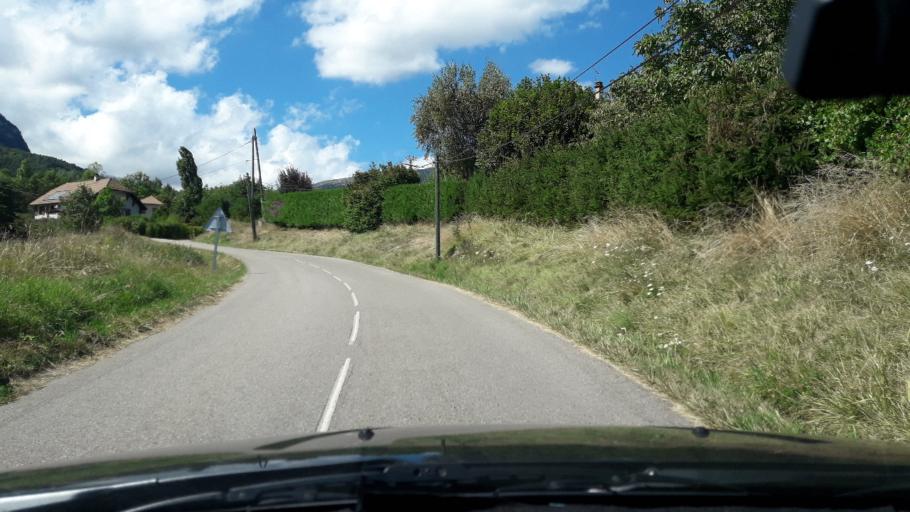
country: FR
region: Rhone-Alpes
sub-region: Departement de l'Isere
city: Mens
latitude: 44.8486
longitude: 5.6240
